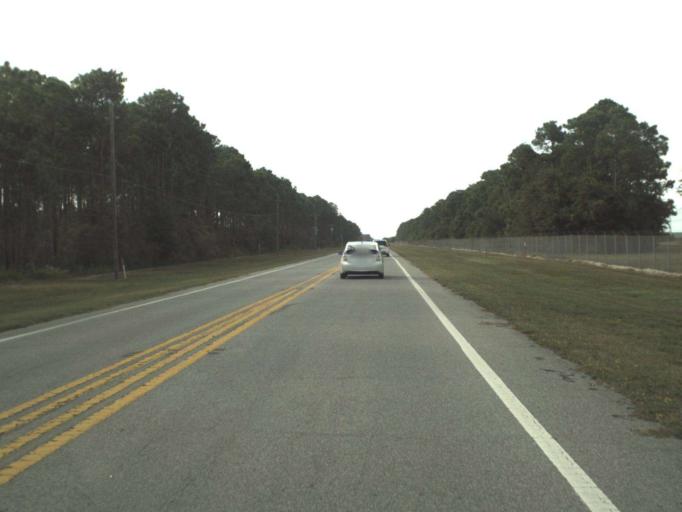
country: US
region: Florida
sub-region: Bay County
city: Tyndall Air Force Base
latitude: 30.0528
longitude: -85.5679
